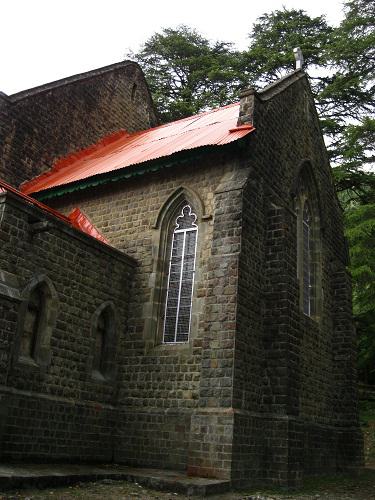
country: IN
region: Himachal Pradesh
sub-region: Kangra
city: Dharmsala
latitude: 32.2425
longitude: 76.3182
